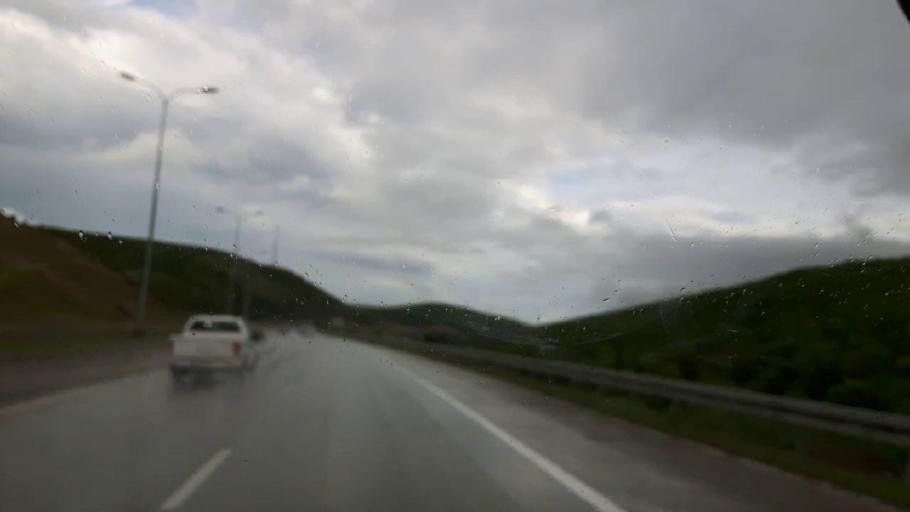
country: GE
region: Shida Kartli
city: Kaspi
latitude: 41.9968
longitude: 44.4011
